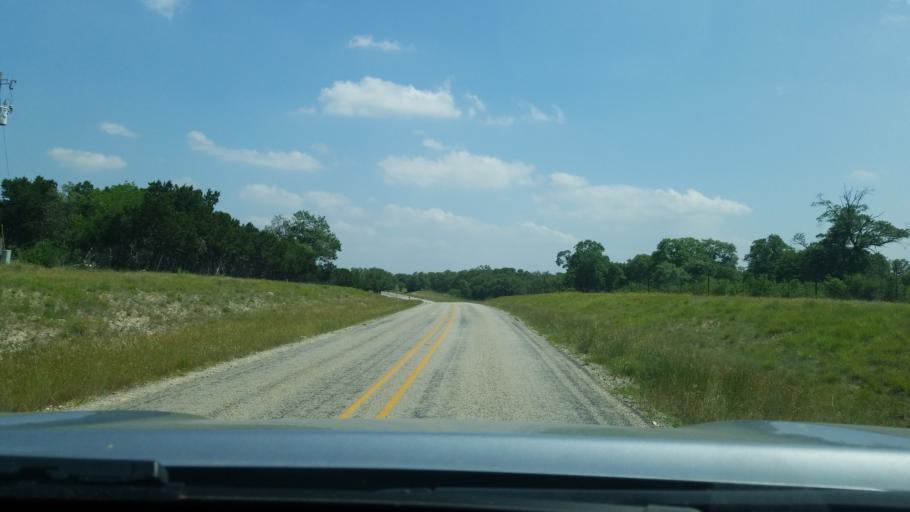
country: US
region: Texas
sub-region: Bexar County
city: Fair Oaks Ranch
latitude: 29.9062
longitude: -98.5683
